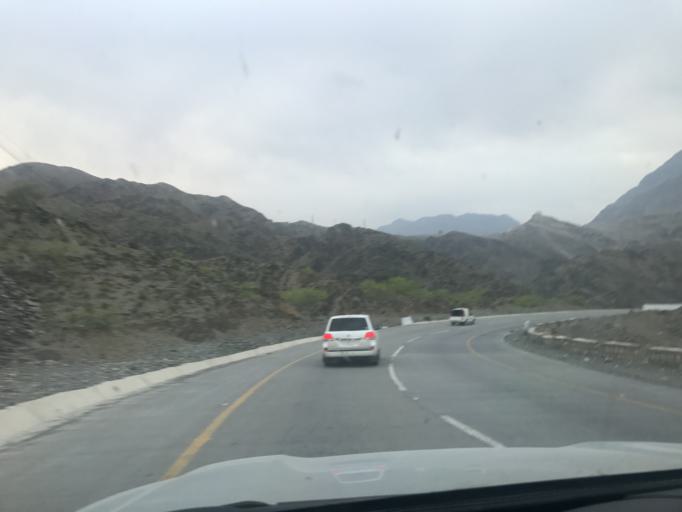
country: PK
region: Federally Administered Tribal Areas
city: Landi Kotal
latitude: 34.0091
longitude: 71.2961
